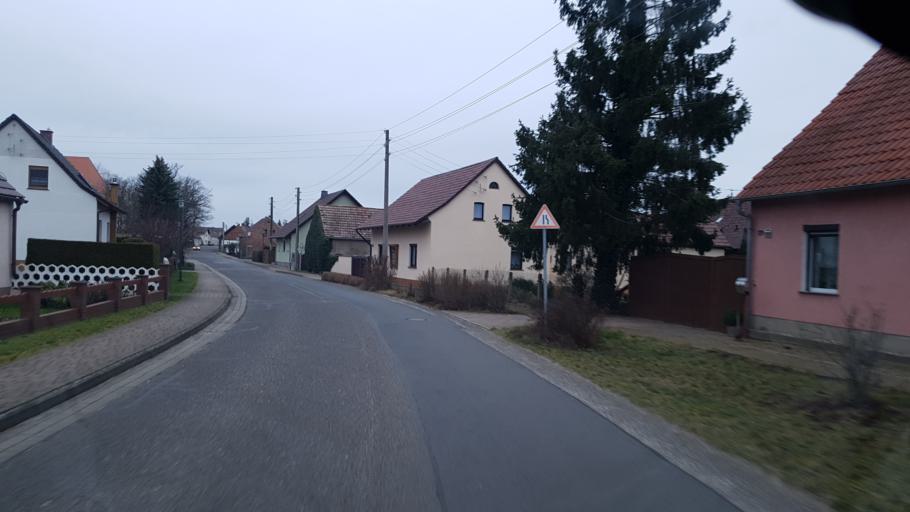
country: DE
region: Brandenburg
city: Schlieben
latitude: 51.7146
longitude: 13.3002
